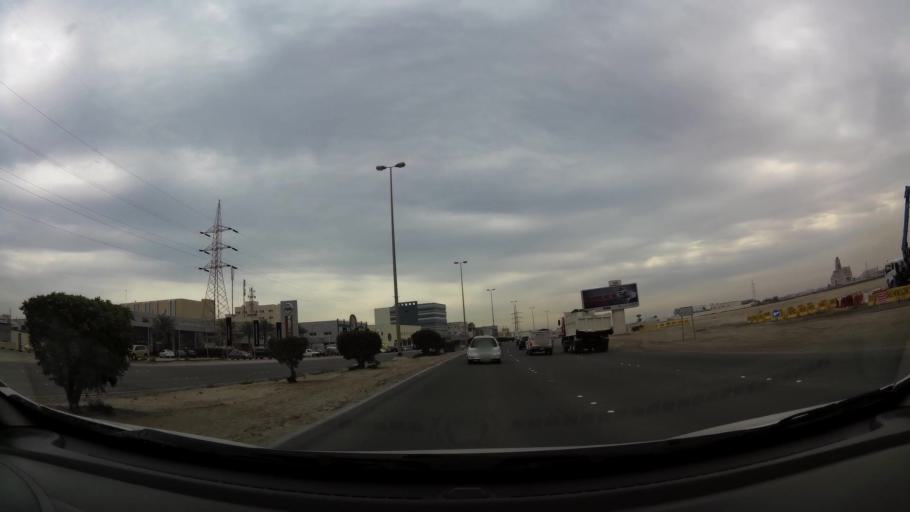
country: BH
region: Northern
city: Sitrah
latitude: 26.1515
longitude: 50.6169
